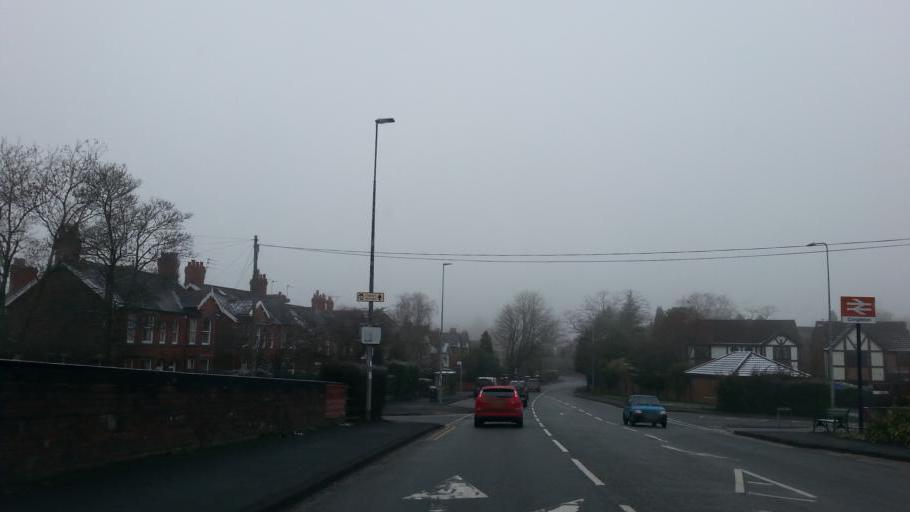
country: GB
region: England
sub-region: Cheshire East
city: Congleton
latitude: 53.1578
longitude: -2.1935
